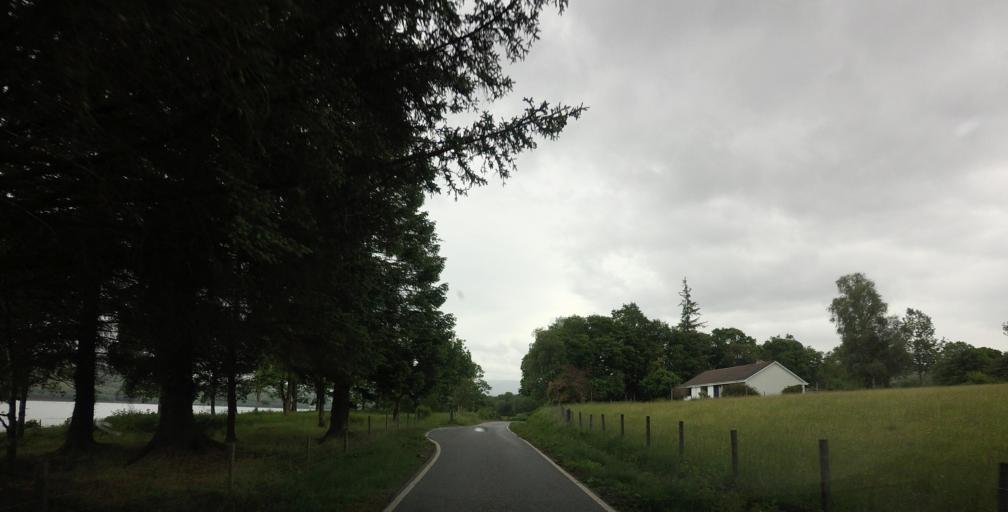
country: GB
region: Scotland
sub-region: Highland
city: Fort William
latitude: 56.8448
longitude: -5.2020
